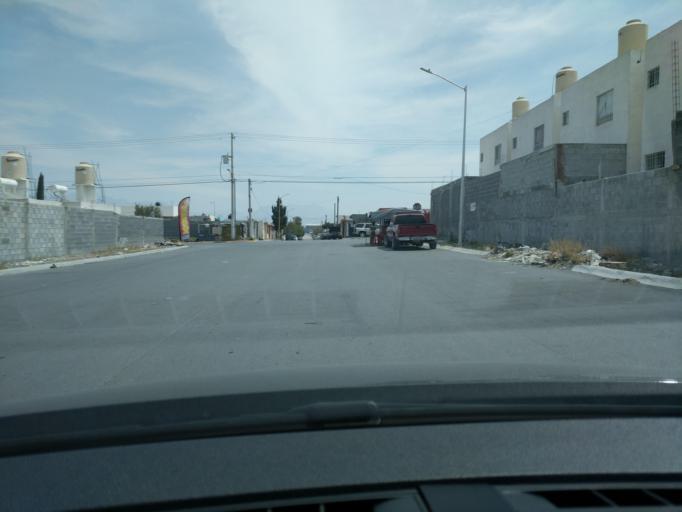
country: MX
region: Coahuila
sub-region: Arteaga
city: Arteaga
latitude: 25.4241
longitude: -100.9111
